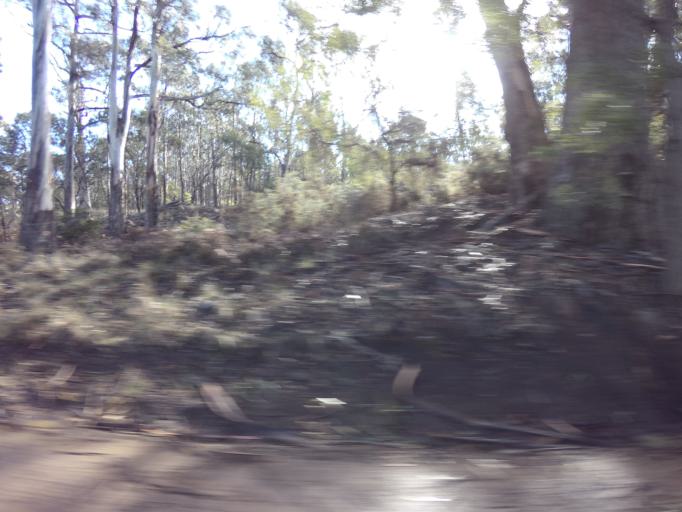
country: AU
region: Tasmania
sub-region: Sorell
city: Sorell
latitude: -42.4126
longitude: 147.9527
